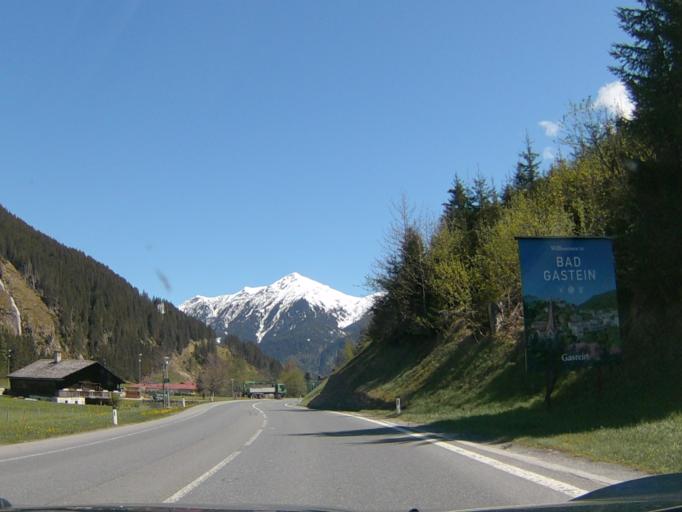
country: AT
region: Salzburg
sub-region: Politischer Bezirk Sankt Johann im Pongau
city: Bad Gastein
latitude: 47.0954
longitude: 13.1239
